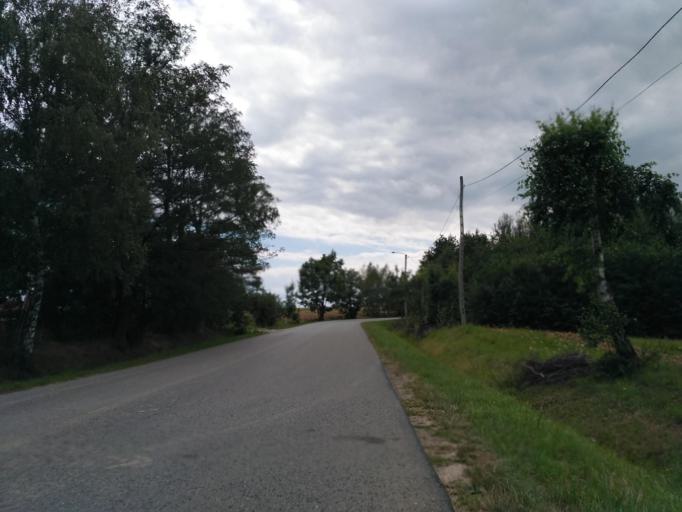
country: PL
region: Subcarpathian Voivodeship
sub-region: Powiat rzeszowski
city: Straszydle
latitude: 49.8843
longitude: 21.9918
